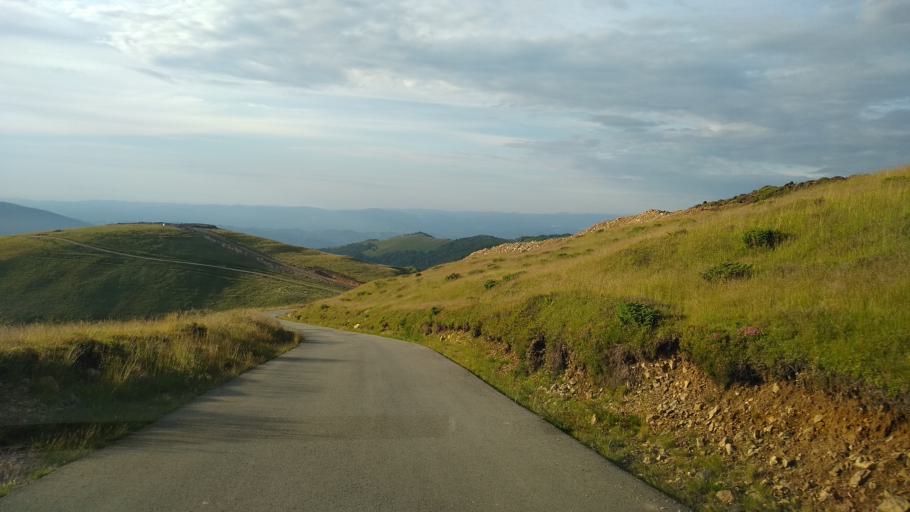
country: RO
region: Hunedoara
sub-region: Municipiul  Vulcan
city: Jiu-Paroseni
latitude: 45.3046
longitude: 23.3122
